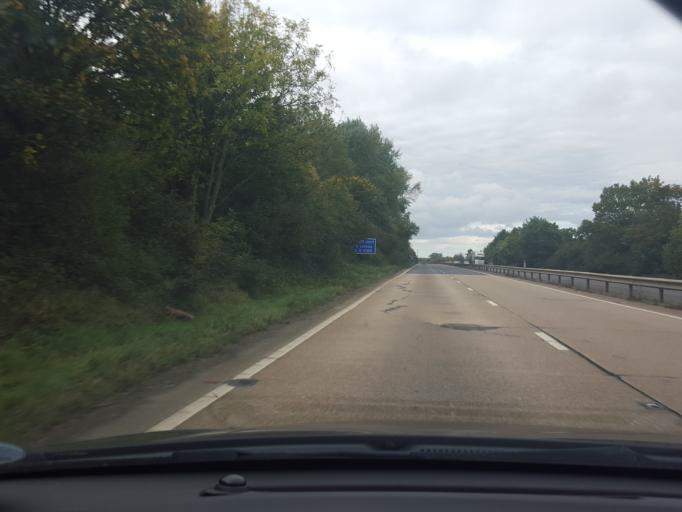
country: GB
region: England
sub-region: Suffolk
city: Woolpit
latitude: 52.2258
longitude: 0.9019
